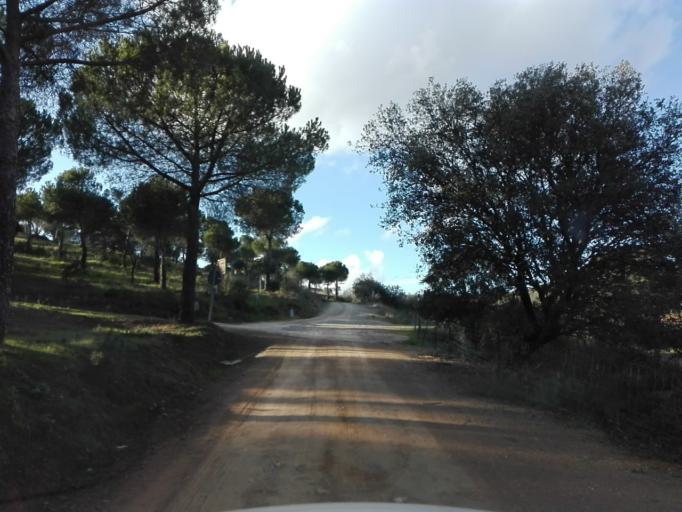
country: ES
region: Extremadura
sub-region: Provincia de Badajoz
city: Trasierra
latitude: 38.1815
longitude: -5.9811
